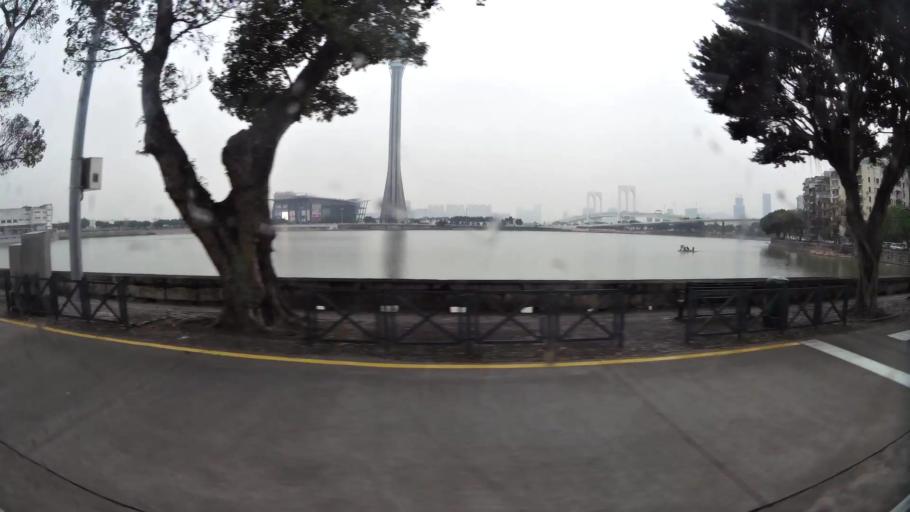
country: CN
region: Guangdong
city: Wanzai
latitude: 22.1840
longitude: 113.5342
